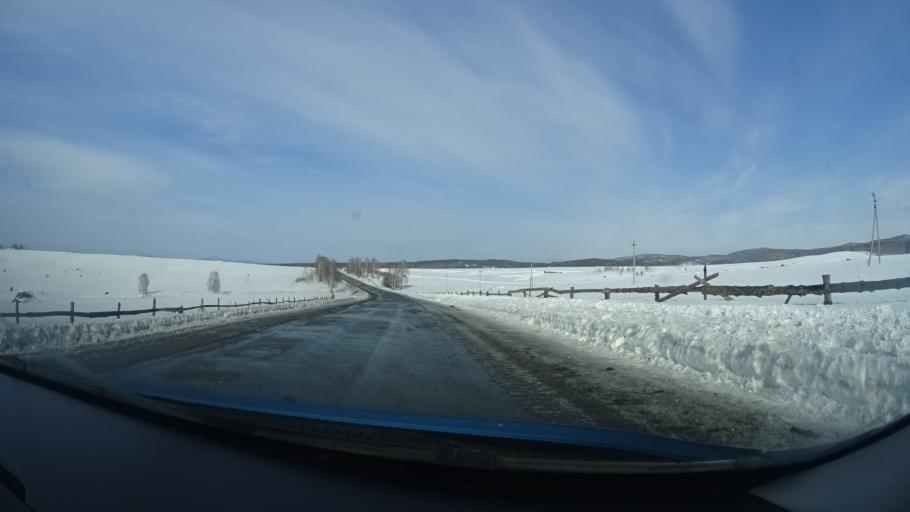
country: RU
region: Bashkortostan
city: Lomovka
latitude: 53.8057
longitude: 58.2710
